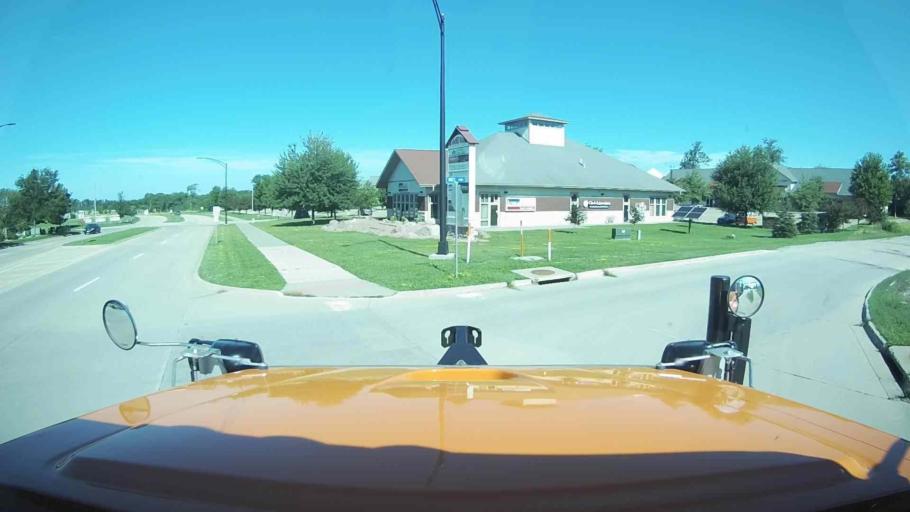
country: US
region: Iowa
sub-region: Johnson County
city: North Liberty
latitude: 41.7086
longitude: -91.6086
